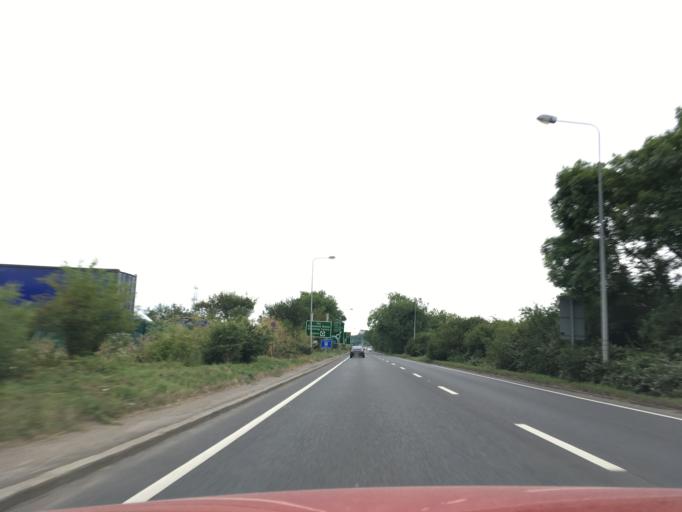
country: GB
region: England
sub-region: Central Bedfordshire
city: Hockliffe
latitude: 51.9139
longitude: -0.5610
